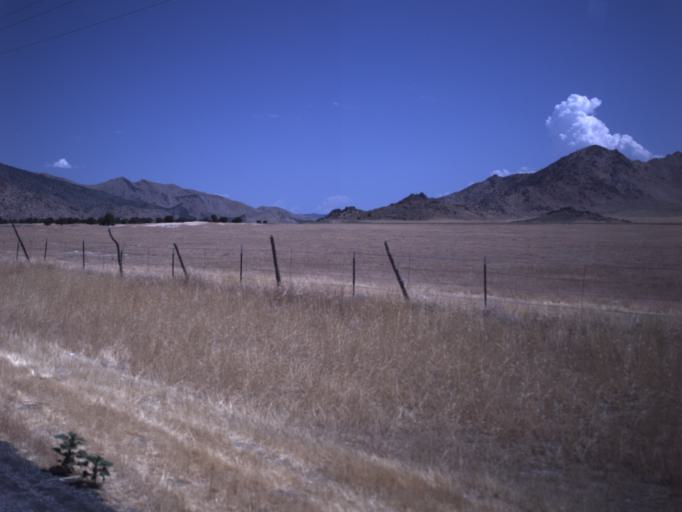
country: US
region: Utah
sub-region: Millard County
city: Delta
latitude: 39.5072
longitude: -112.2690
